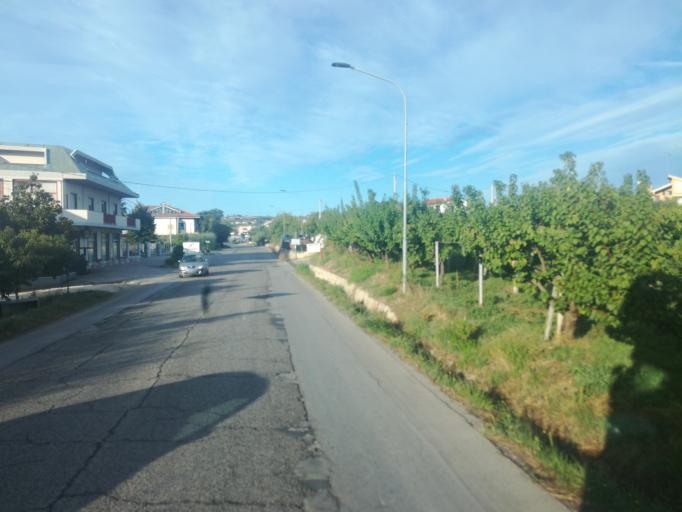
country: IT
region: Abruzzo
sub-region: Provincia di Chieti
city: Miglianico
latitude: 42.3688
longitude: 14.2895
